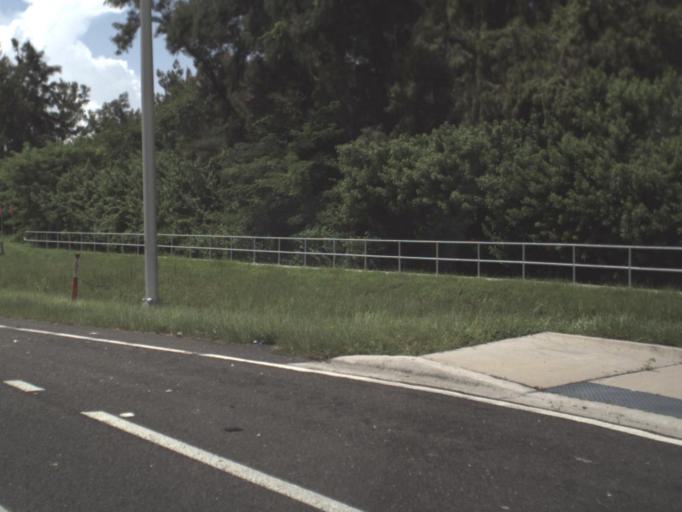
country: US
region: Florida
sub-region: Hillsborough County
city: Progress Village
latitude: 27.9186
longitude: -82.3494
